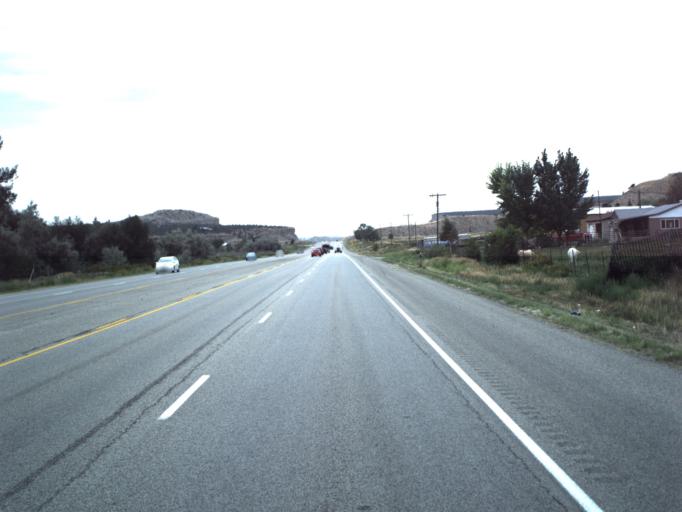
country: US
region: Utah
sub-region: Carbon County
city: Spring Glen
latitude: 39.6617
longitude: -110.8610
